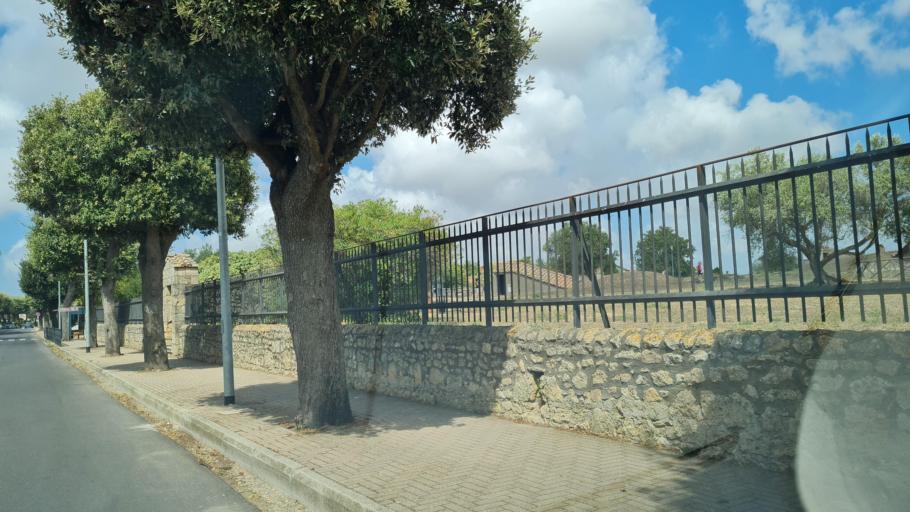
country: IT
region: Latium
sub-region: Provincia di Viterbo
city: Tarquinia
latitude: 42.2495
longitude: 11.7687
